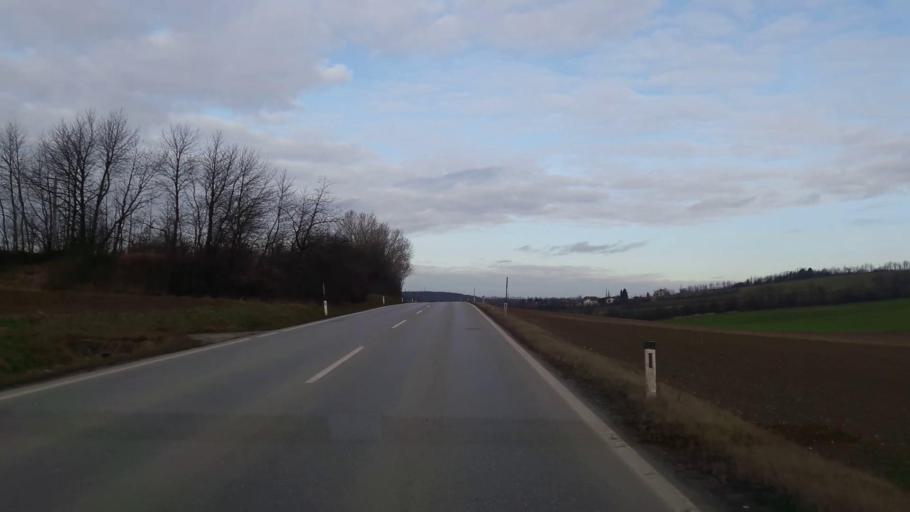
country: AT
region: Lower Austria
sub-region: Politischer Bezirk Mistelbach
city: Asparn an der Zaya
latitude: 48.6159
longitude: 16.5248
